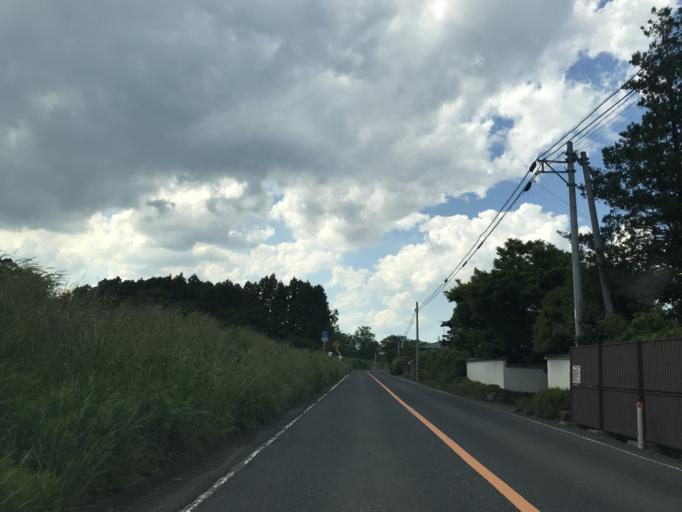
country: JP
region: Miyagi
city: Wakuya
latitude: 38.6553
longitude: 141.2130
